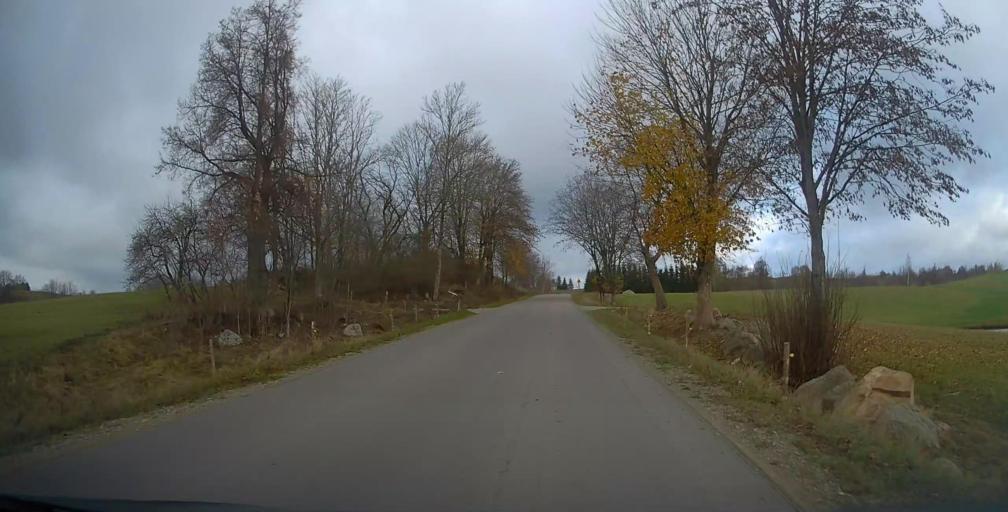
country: PL
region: Podlasie
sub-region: Suwalki
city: Suwalki
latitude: 54.3130
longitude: 22.8789
